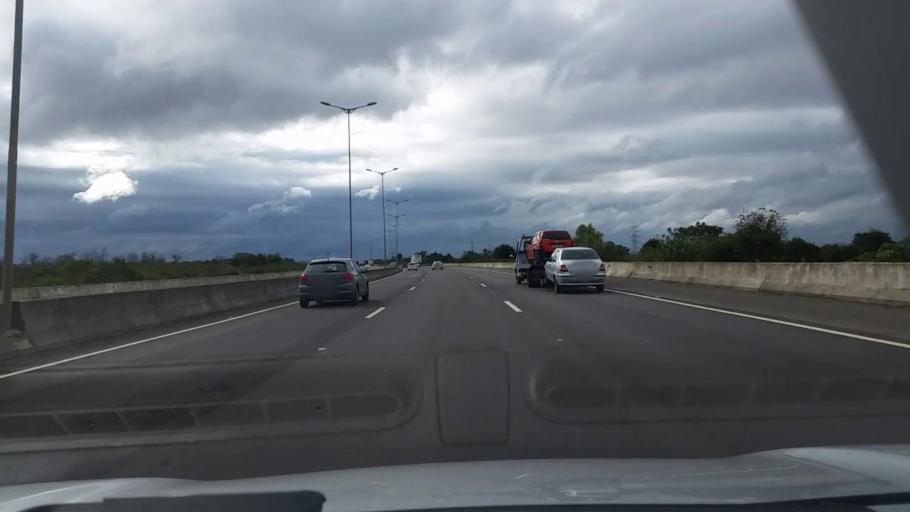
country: BR
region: Rio Grande do Sul
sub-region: Canoas
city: Canoas
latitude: -29.9430
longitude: -51.2048
